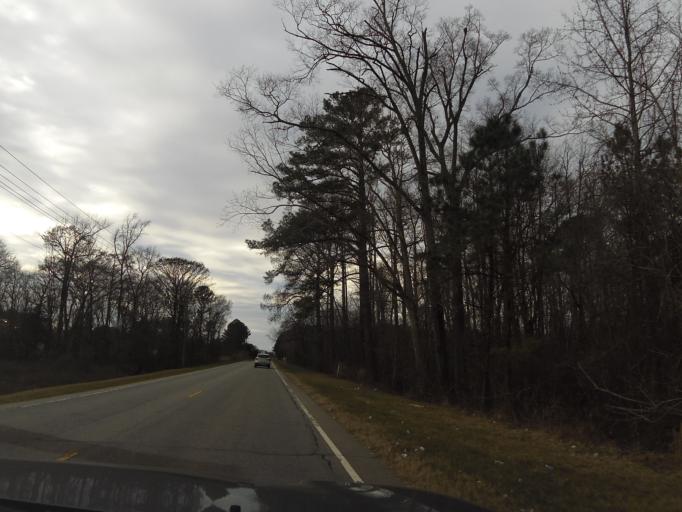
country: US
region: North Carolina
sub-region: Nash County
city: Rocky Mount
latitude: 35.9645
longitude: -77.6735
